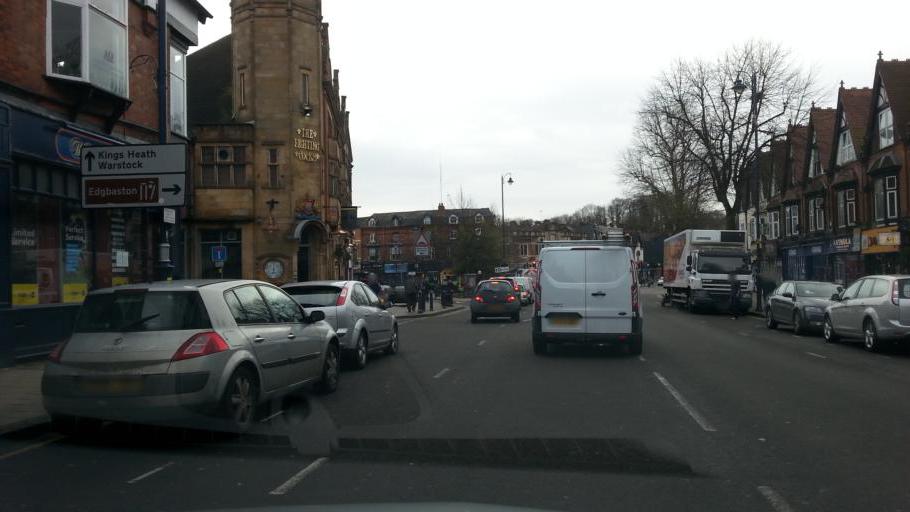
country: GB
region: England
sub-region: City and Borough of Birmingham
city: Birmingham
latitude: 52.4474
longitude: -1.8881
